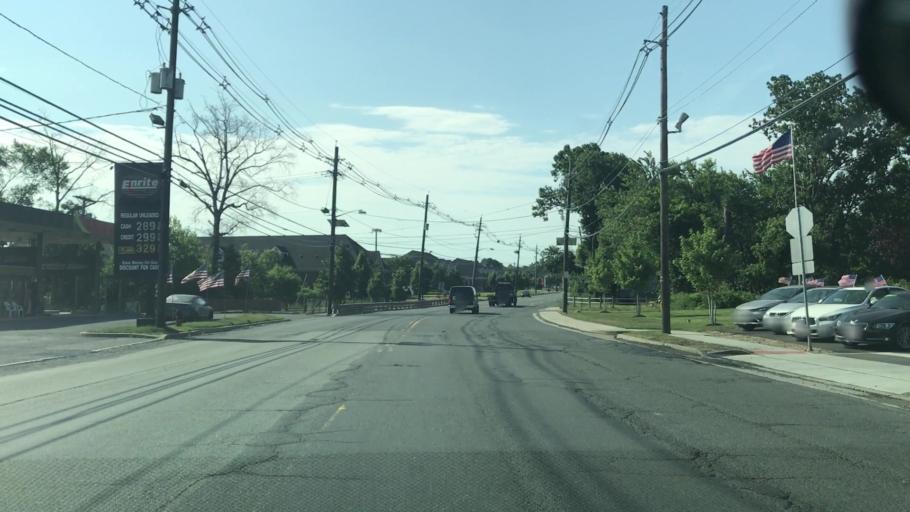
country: US
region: New Jersey
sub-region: Middlesex County
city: South Plainfield
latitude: 40.5584
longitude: -74.4167
